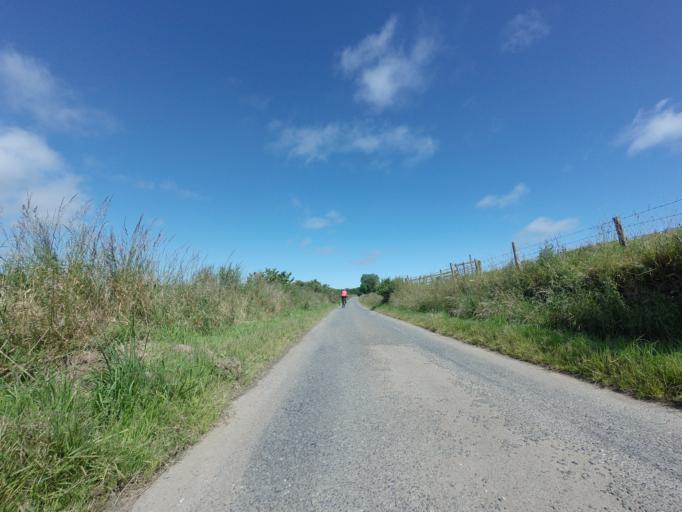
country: GB
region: Scotland
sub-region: Aberdeenshire
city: Banff
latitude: 57.6028
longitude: -2.5125
